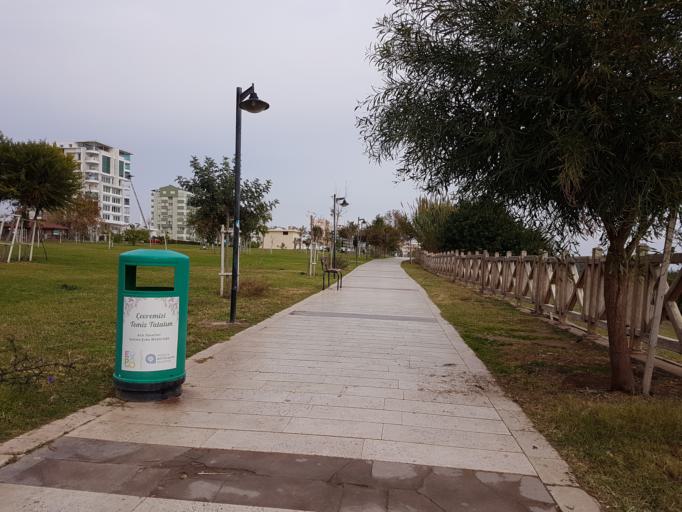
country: TR
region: Antalya
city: Antalya
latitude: 36.8517
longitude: 30.7851
